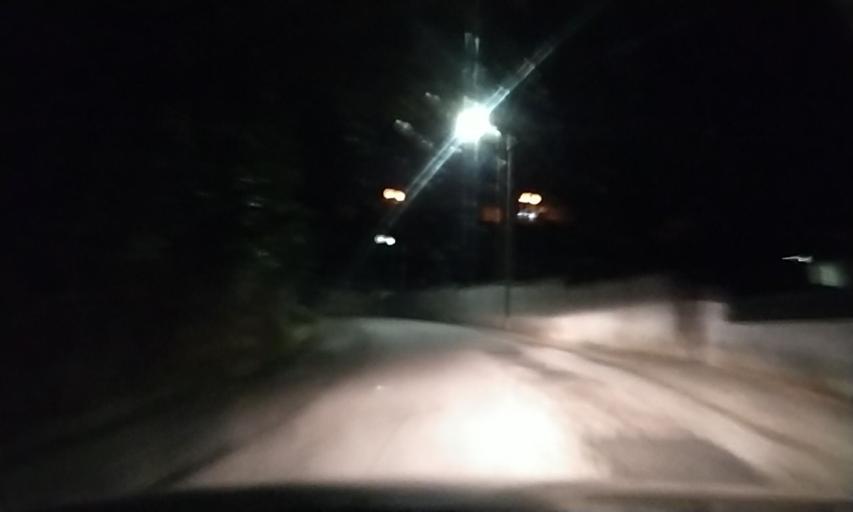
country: PT
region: Vila Real
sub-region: Santa Marta de Penaguiao
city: Santa Marta de Penaguiao
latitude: 41.1921
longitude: -7.8149
